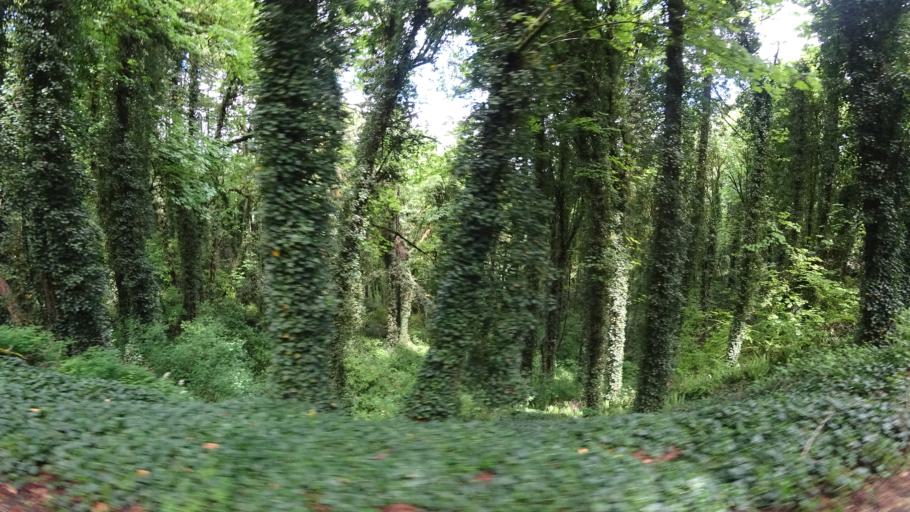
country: US
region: Oregon
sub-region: Washington County
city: West Slope
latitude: 45.5045
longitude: -122.7205
